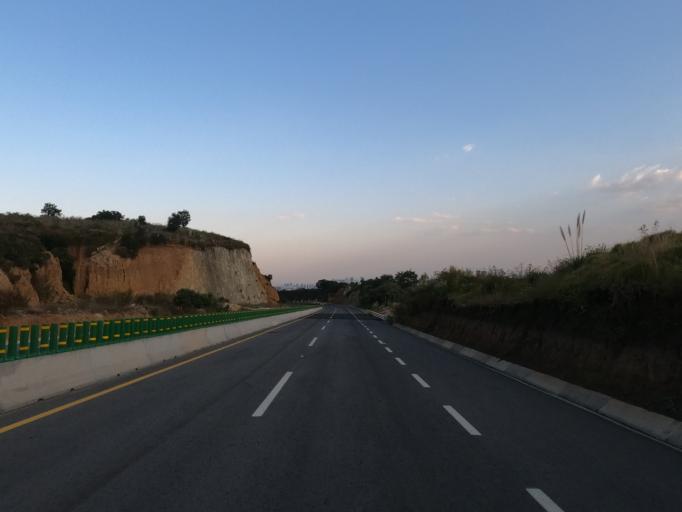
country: MX
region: Mexico
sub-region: Naucalpan de Juarez
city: Llano de las Flores (Barrio del Hueso)
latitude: 19.4213
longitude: -99.3179
